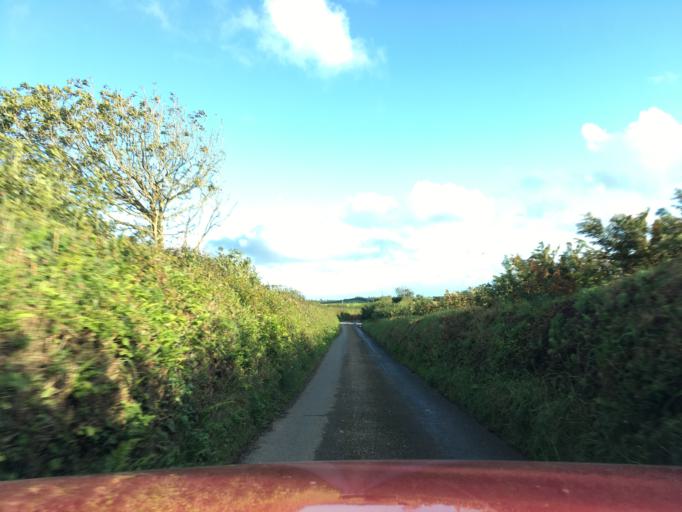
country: GB
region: England
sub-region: Devon
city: Dartmouth
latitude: 50.3454
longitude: -3.6110
